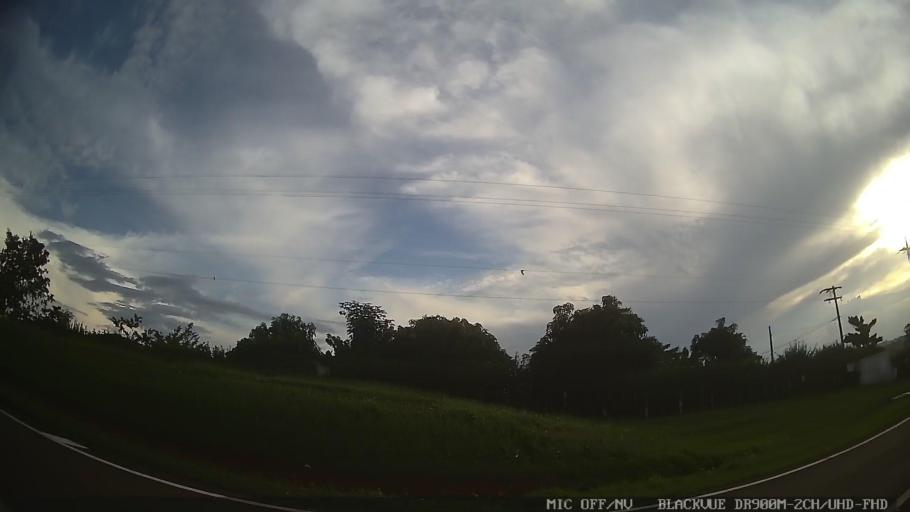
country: BR
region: Sao Paulo
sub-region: Porto Feliz
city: Porto Feliz
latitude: -23.1968
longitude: -47.6181
